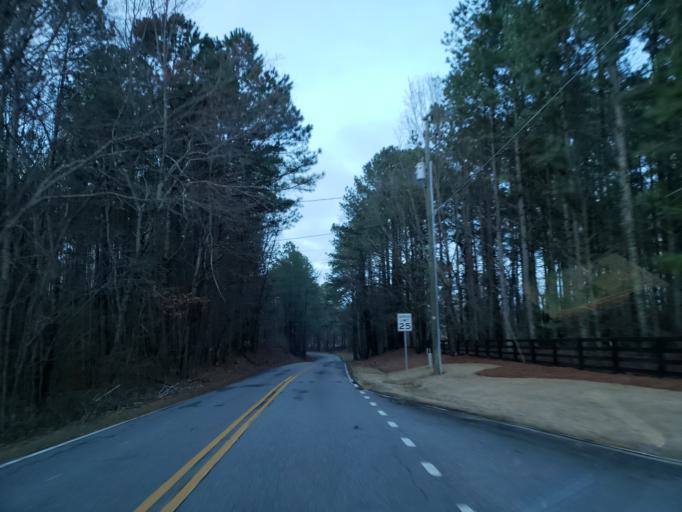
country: US
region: Georgia
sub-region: Cherokee County
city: Ball Ground
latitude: 34.2408
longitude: -84.3354
